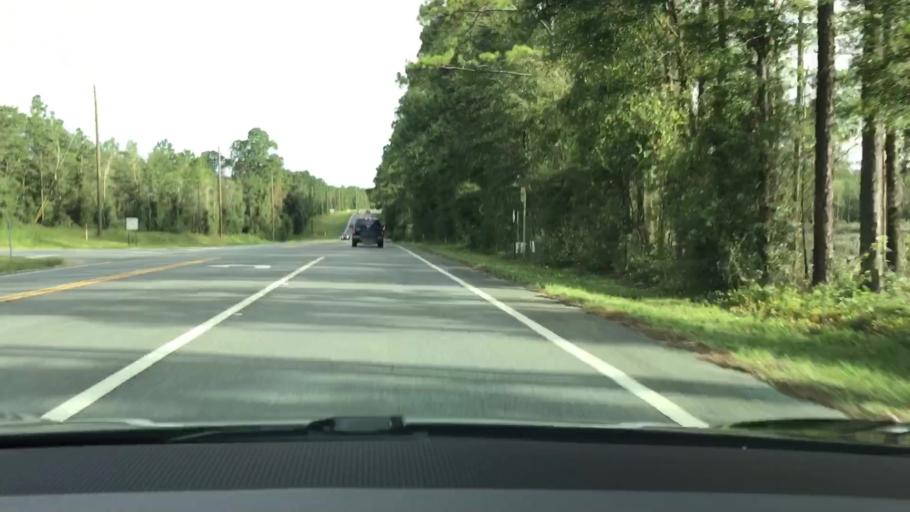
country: US
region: Florida
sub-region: Walton County
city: DeFuniak Springs
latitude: 30.7755
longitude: -86.1147
